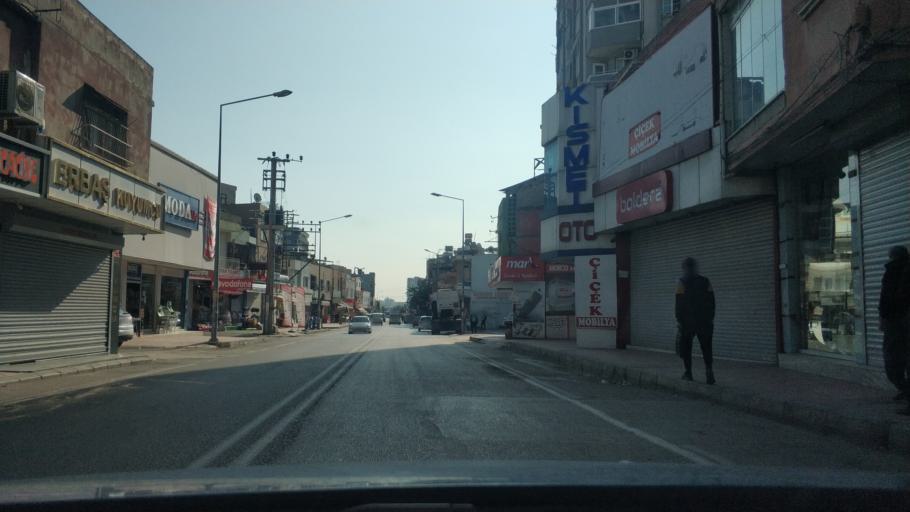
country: TR
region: Adana
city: Seyhan
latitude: 37.0182
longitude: 35.2984
